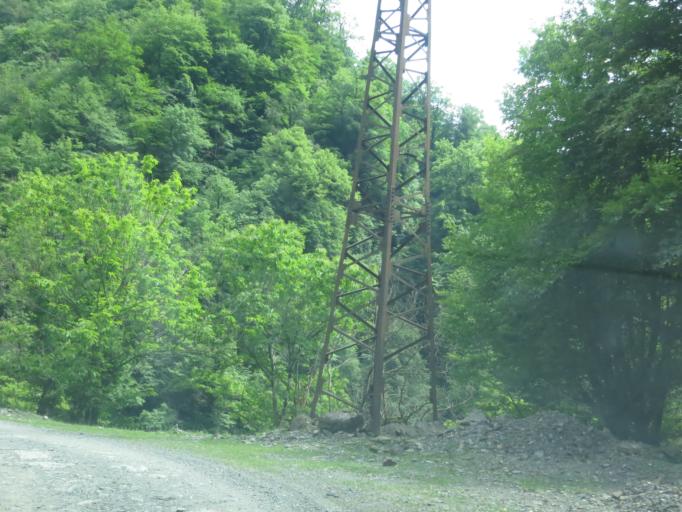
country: GE
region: Kakheti
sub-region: Telavi
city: Telavi
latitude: 42.2040
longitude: 45.4641
